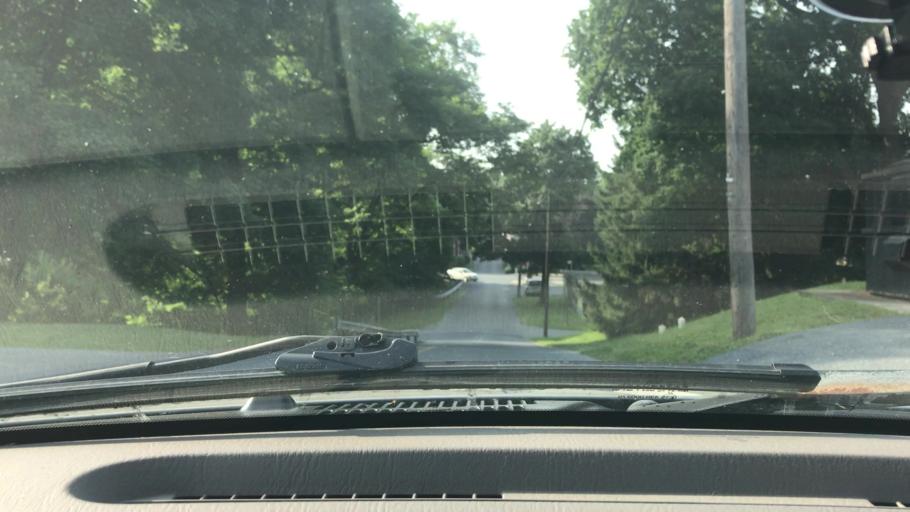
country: US
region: Pennsylvania
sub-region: Lancaster County
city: Elizabethtown
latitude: 40.1481
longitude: -76.6028
